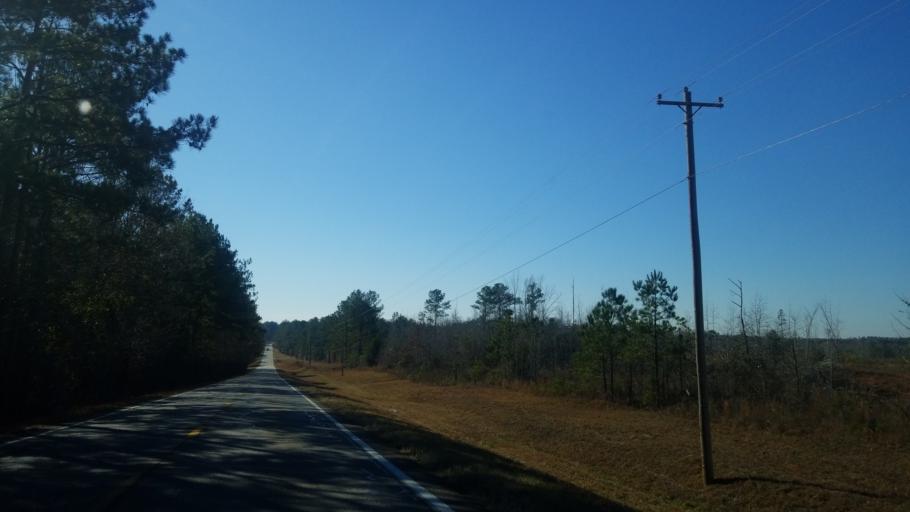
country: US
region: Georgia
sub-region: Harris County
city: Hamilton
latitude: 32.7095
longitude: -85.0230
